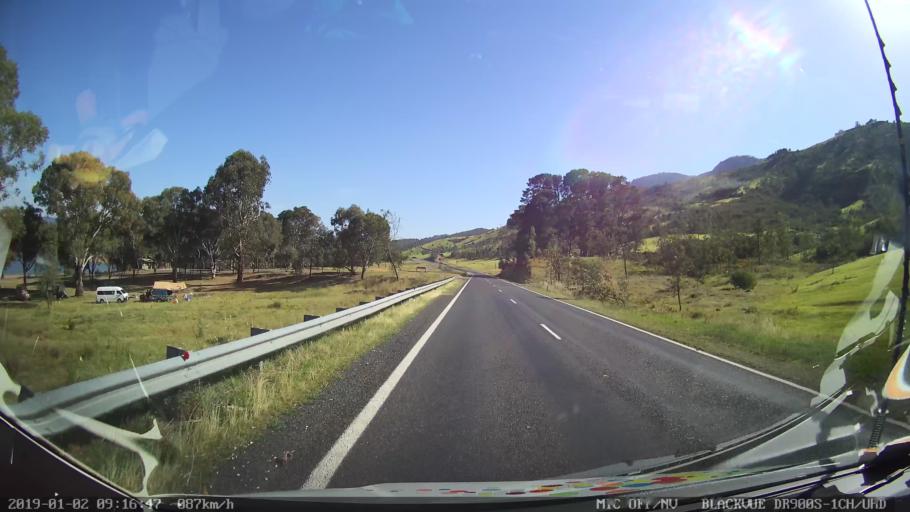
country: AU
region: New South Wales
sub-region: Tumut Shire
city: Tumut
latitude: -35.4492
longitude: 148.2852
